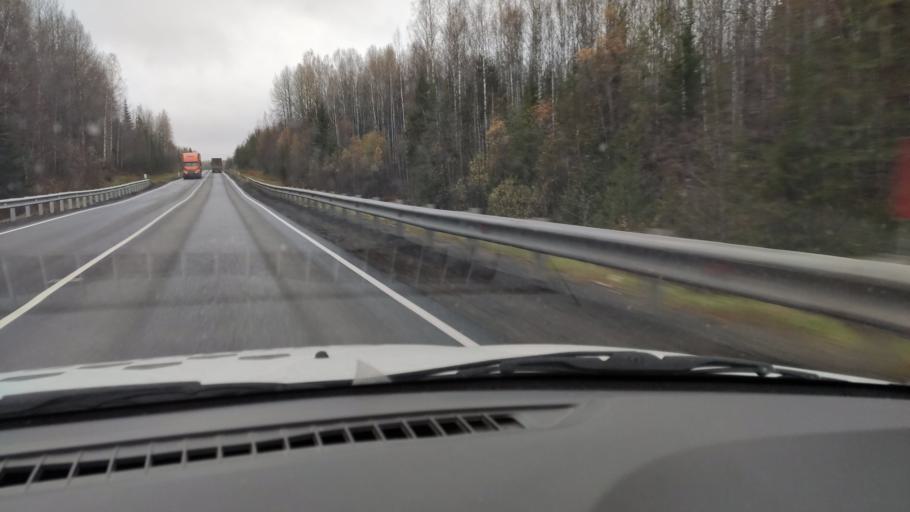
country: RU
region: Kirov
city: Omutninsk
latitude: 58.7392
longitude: 52.0690
